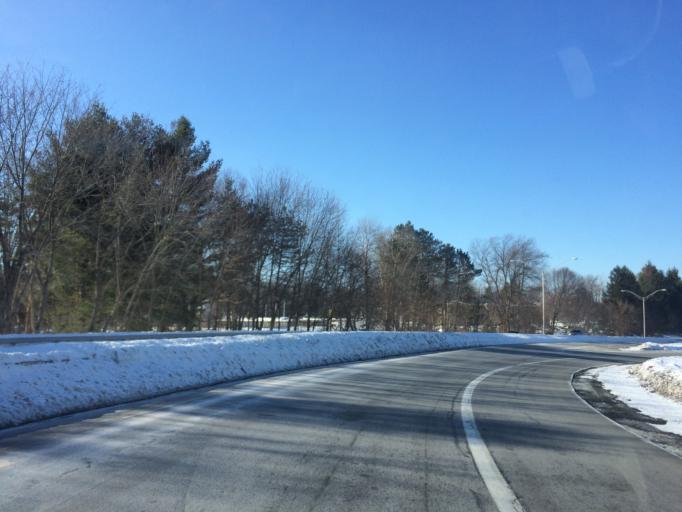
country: US
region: New York
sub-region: Monroe County
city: Pittsford
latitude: 43.1100
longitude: -77.5085
